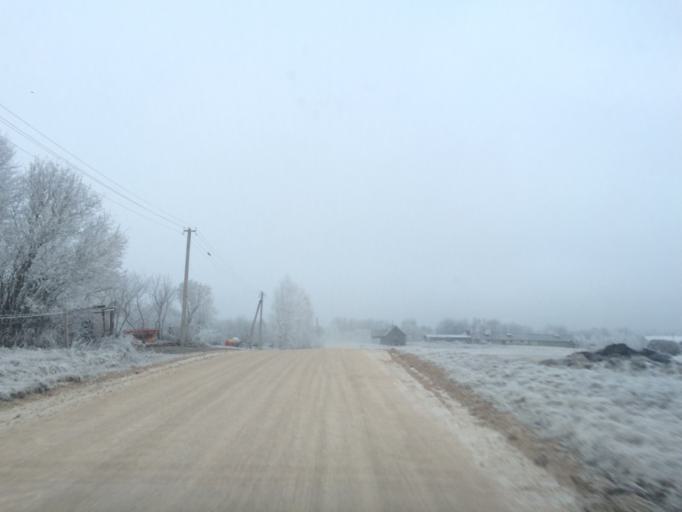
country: LV
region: Ludzas Rajons
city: Ludza
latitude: 56.6207
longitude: 27.5194
